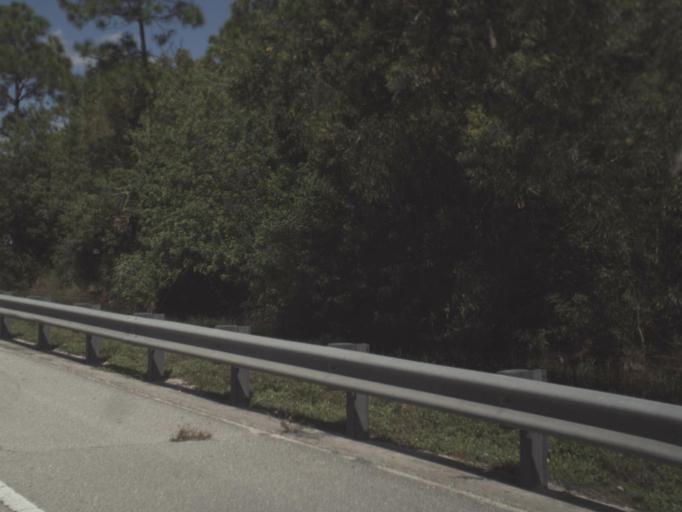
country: US
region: Florida
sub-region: Collier County
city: Lely Resort
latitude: 26.0345
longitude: -81.6539
